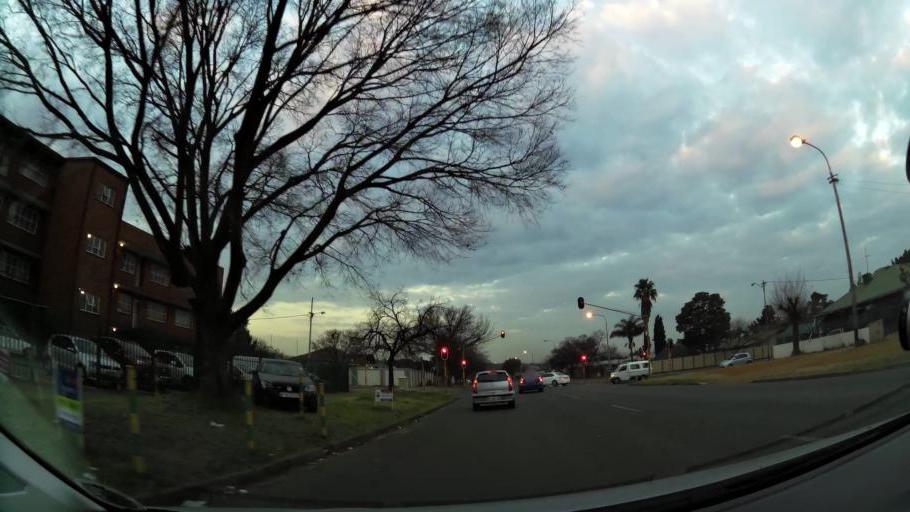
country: ZA
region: Gauteng
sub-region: Ekurhuleni Metropolitan Municipality
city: Germiston
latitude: -26.1988
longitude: 28.1265
